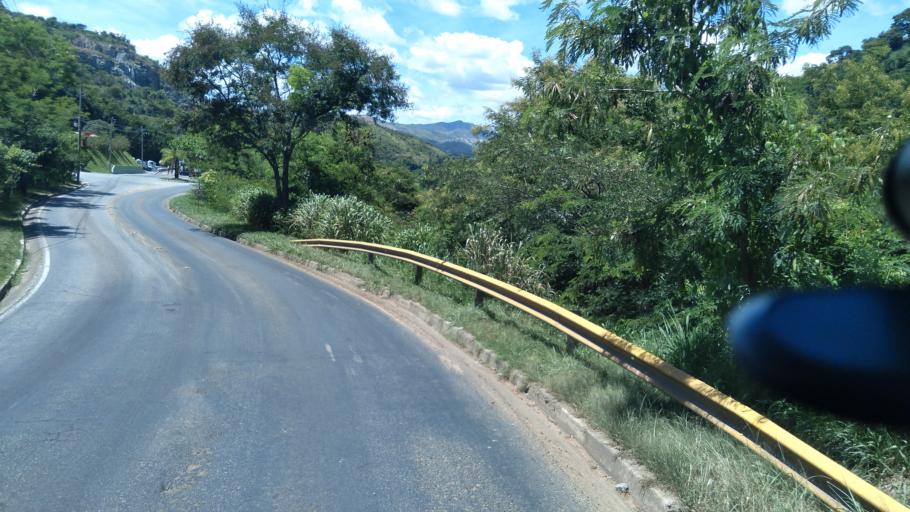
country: BR
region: Minas Gerais
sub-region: Santa Luzia
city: Santa Luzia
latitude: -19.8610
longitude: -43.8519
